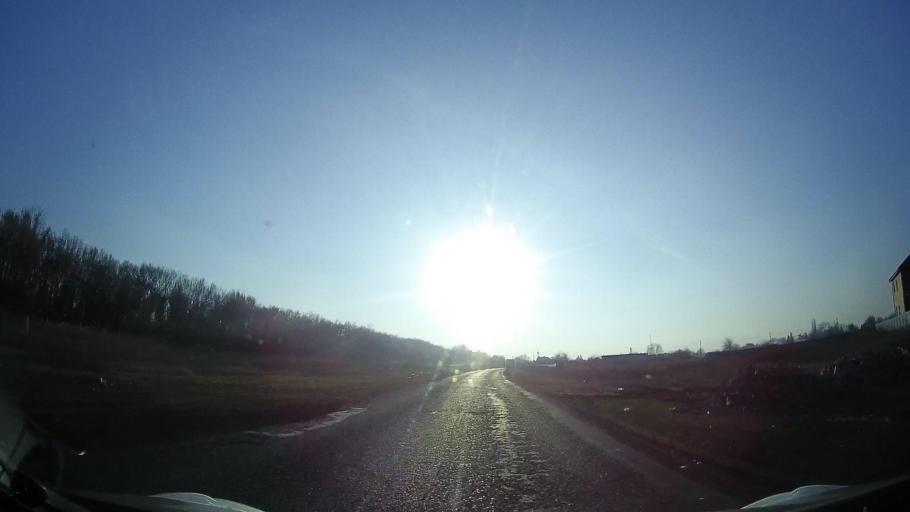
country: RU
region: Rostov
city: Ol'ginskaya
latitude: 47.1360
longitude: 39.8934
